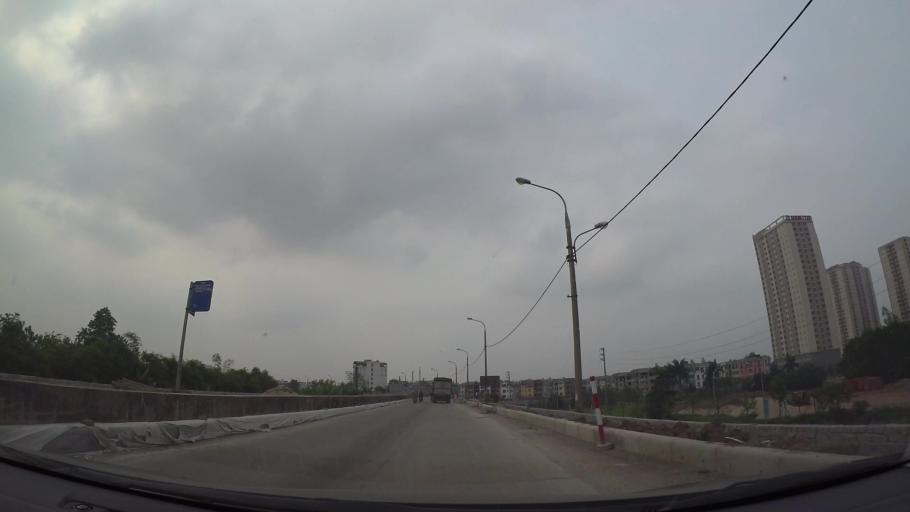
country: VN
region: Ha Noi
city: Trau Quy
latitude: 21.0170
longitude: 105.9045
